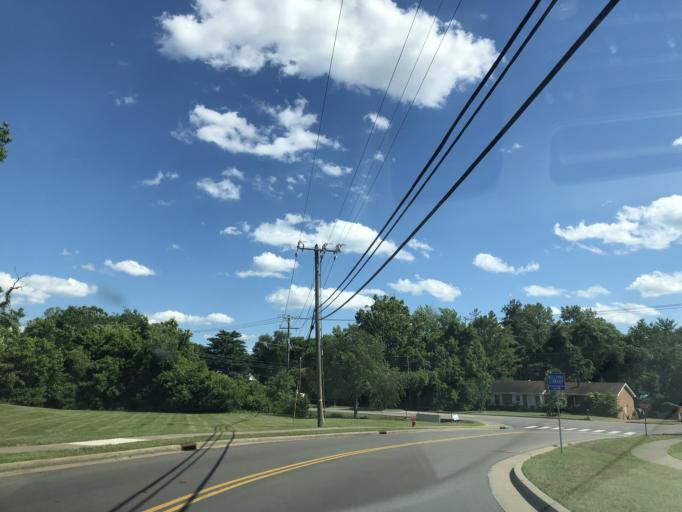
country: US
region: Tennessee
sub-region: Davidson County
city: Belle Meade
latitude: 36.0698
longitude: -86.9335
